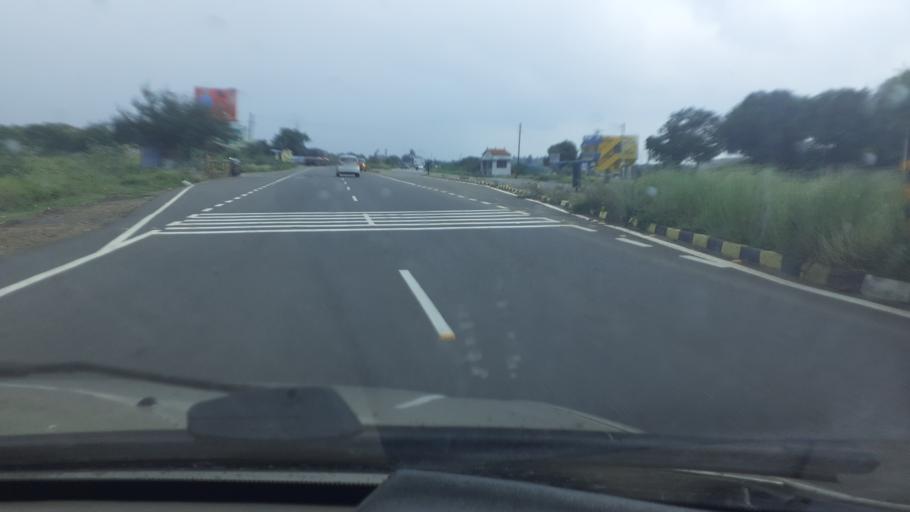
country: IN
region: Tamil Nadu
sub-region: Virudhunagar
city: Virudunagar
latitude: 9.6522
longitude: 77.9659
